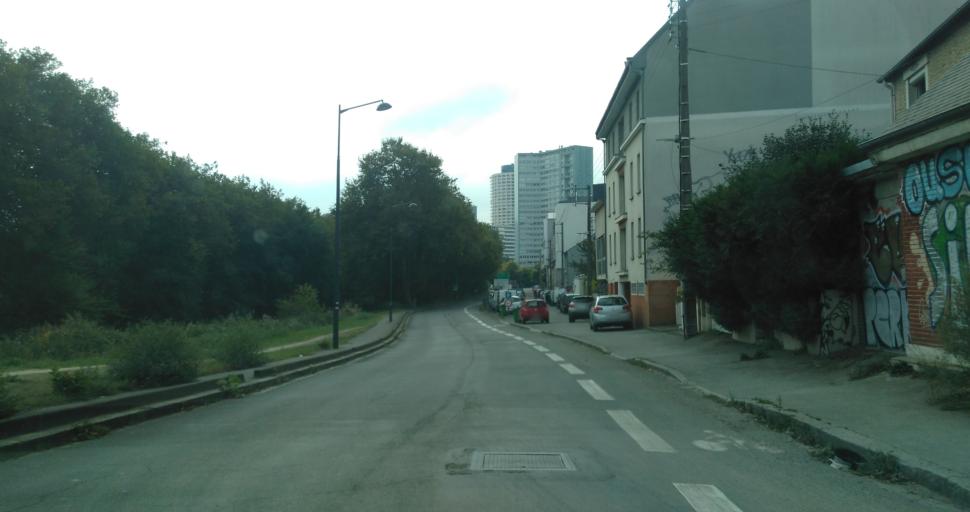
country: FR
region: Brittany
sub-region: Departement d'Ille-et-Vilaine
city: Rennes
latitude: 48.1176
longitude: -1.6864
